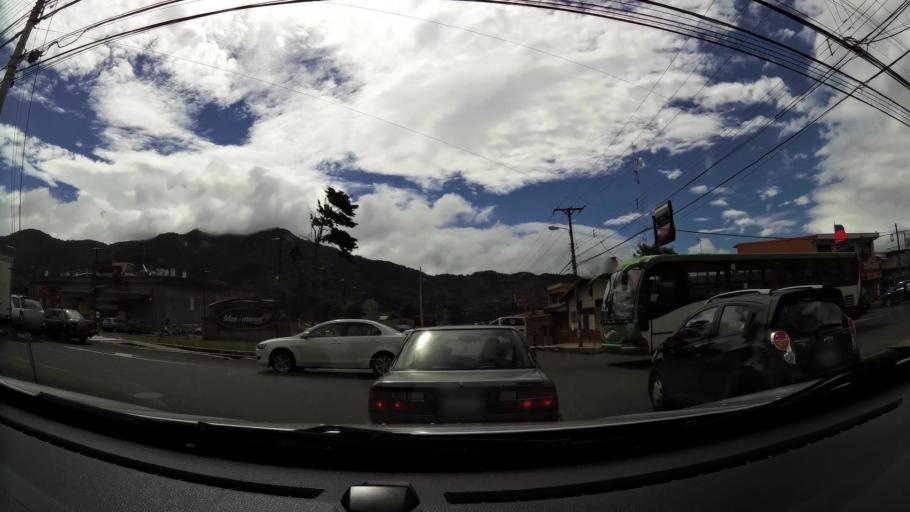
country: CR
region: Cartago
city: Tres Rios
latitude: 9.9090
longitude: -83.9892
